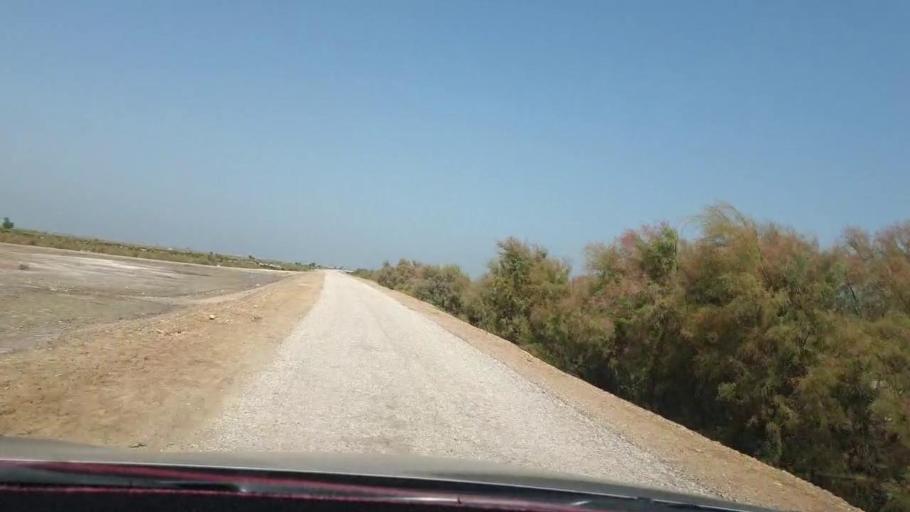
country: PK
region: Sindh
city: Warah
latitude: 27.5266
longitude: 67.7112
